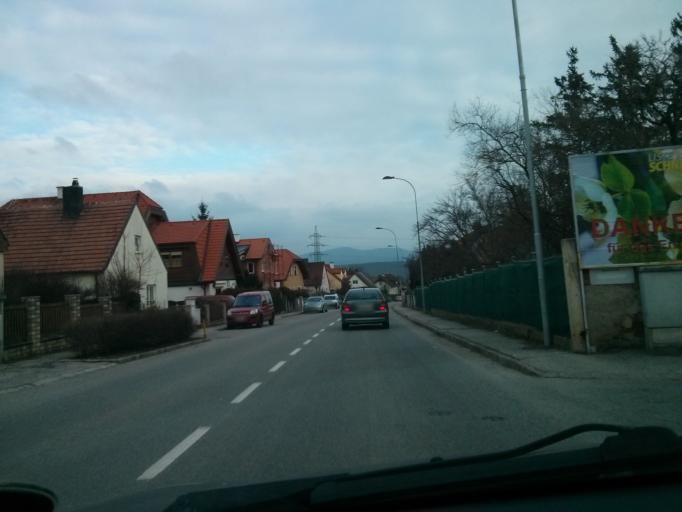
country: AT
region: Lower Austria
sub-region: Politischer Bezirk Baden
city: Hirtenberg
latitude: 47.9153
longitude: 16.1881
